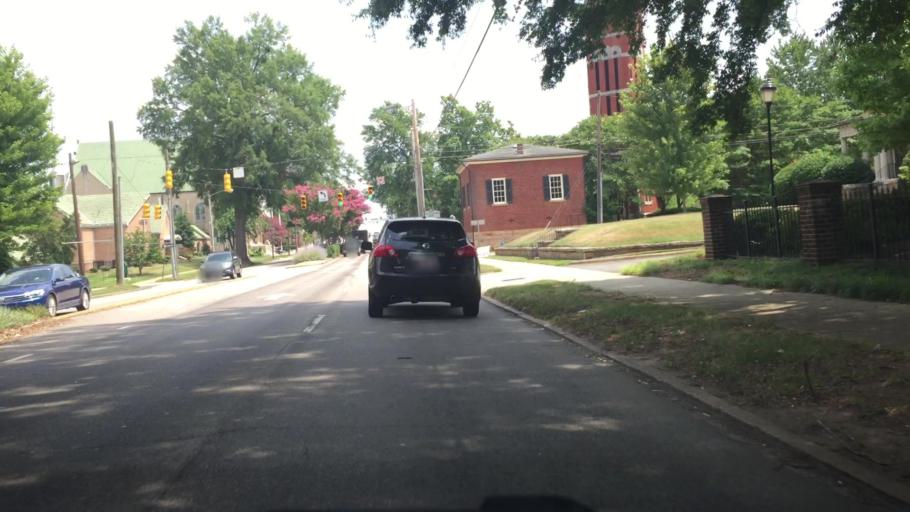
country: US
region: North Carolina
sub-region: Rowan County
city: Salisbury
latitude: 35.6696
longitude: -80.4726
